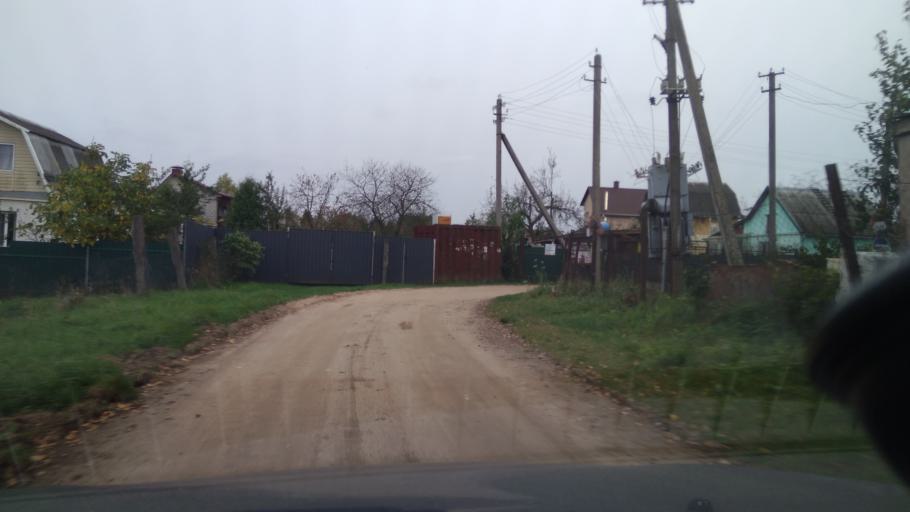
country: BY
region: Minsk
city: Rudzyensk
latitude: 53.6061
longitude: 27.8486
